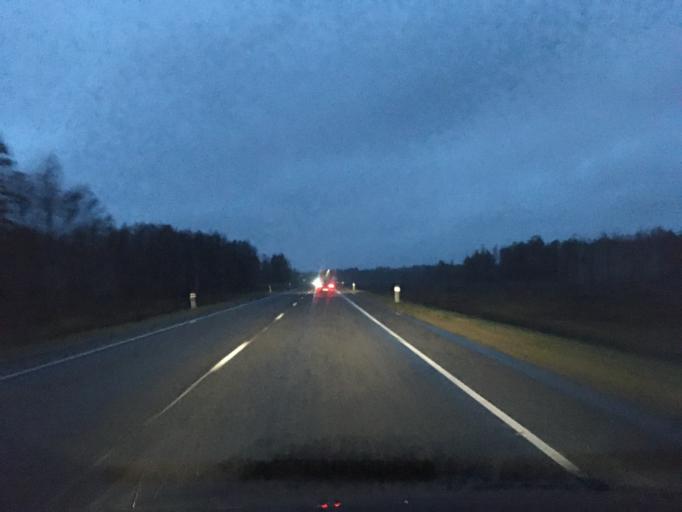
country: EE
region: Harju
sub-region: Nissi vald
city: Turba
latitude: 58.9870
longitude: 24.0580
